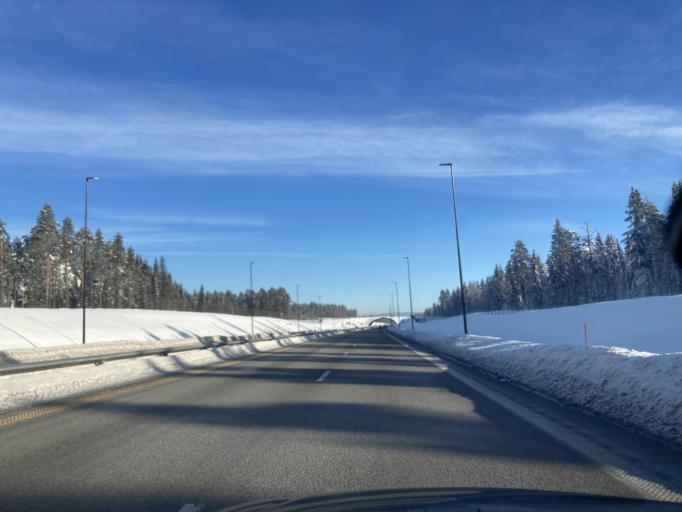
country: NO
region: Hedmark
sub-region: Loten
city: Loten
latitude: 60.8572
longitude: 11.4026
